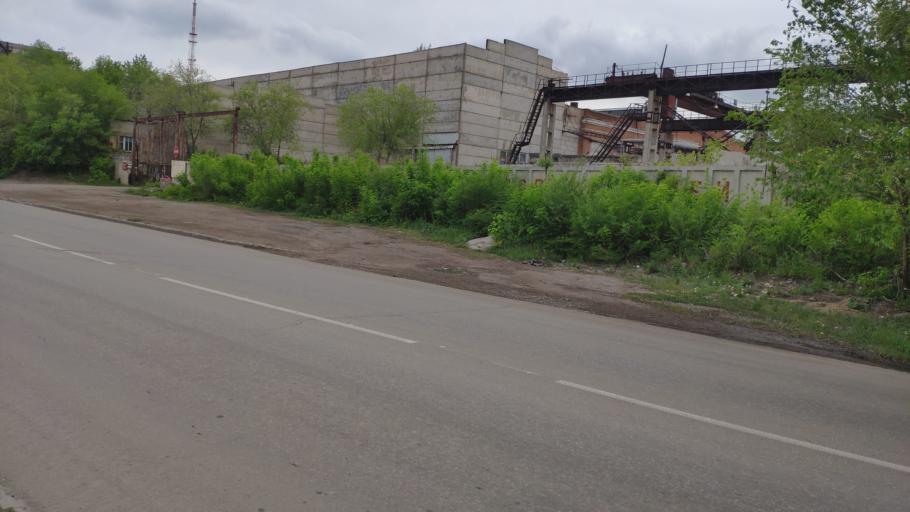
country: RU
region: Chelyabinsk
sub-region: Gorod Magnitogorsk
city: Magnitogorsk
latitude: 53.4149
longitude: 58.9562
